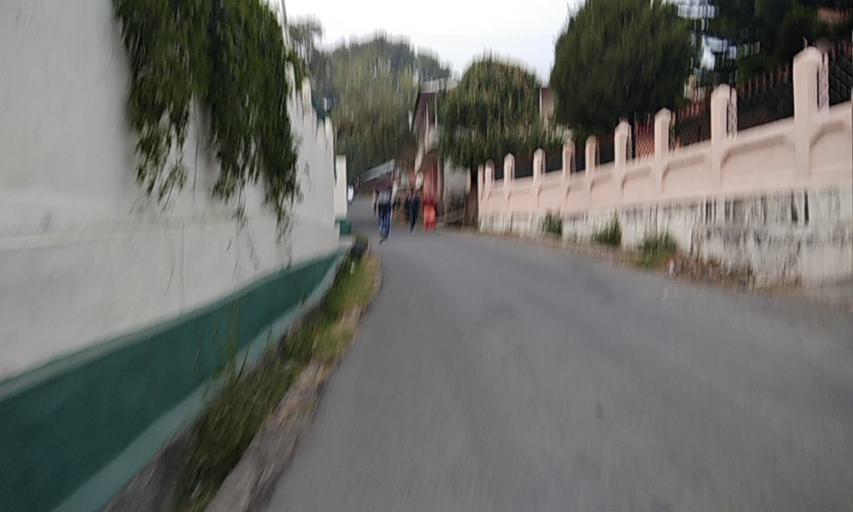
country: IN
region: Himachal Pradesh
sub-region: Kangra
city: Palampur
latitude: 32.1177
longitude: 76.5328
